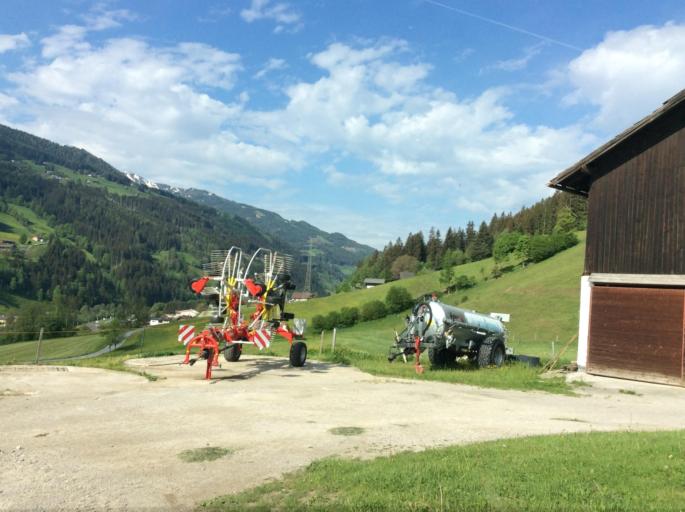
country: AT
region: Styria
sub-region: Politischer Bezirk Liezen
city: Schladming
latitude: 47.3940
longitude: 13.6616
